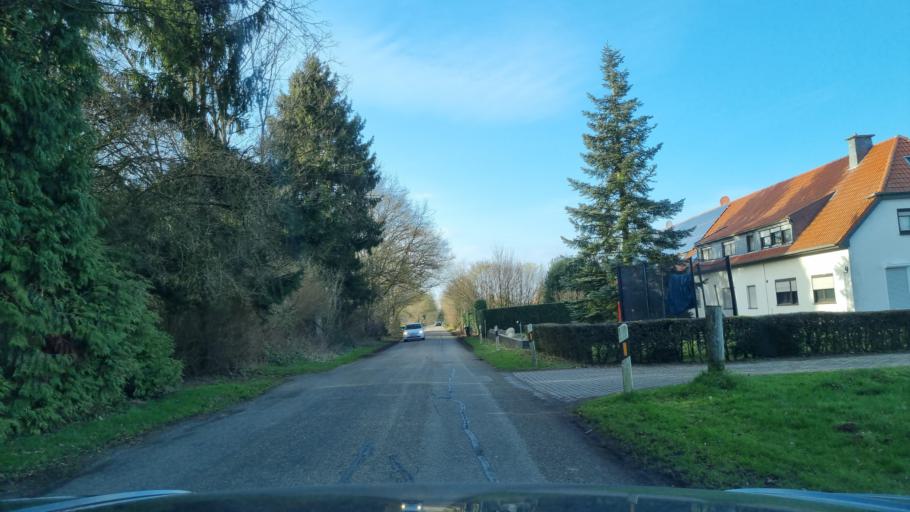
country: DE
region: North Rhine-Westphalia
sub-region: Regierungsbezirk Dusseldorf
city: Kleve
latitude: 51.7487
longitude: 6.1186
